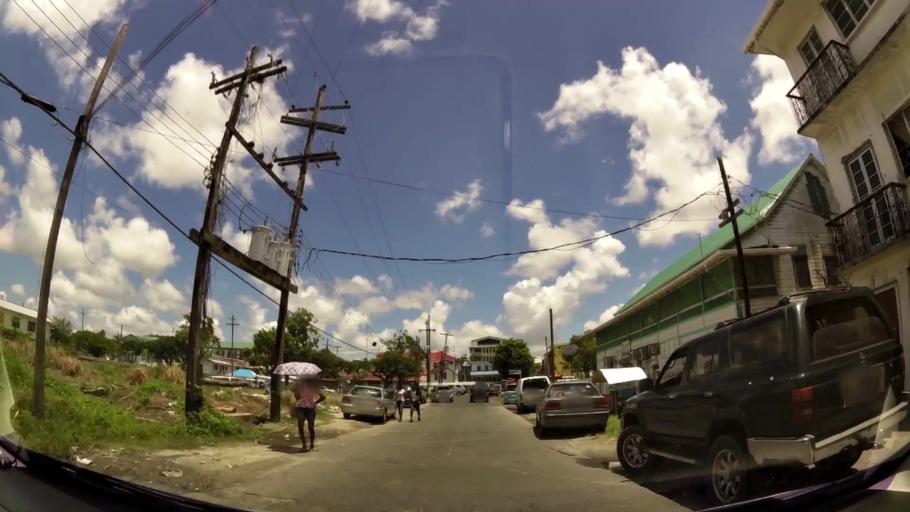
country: GY
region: Demerara-Mahaica
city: Georgetown
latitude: 6.8095
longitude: -58.1628
